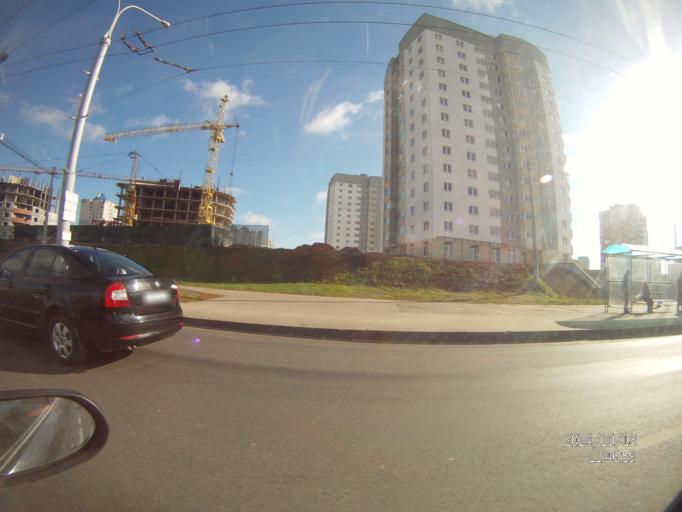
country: BY
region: Minsk
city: Novoye Medvezhino
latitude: 53.8725
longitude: 27.4768
